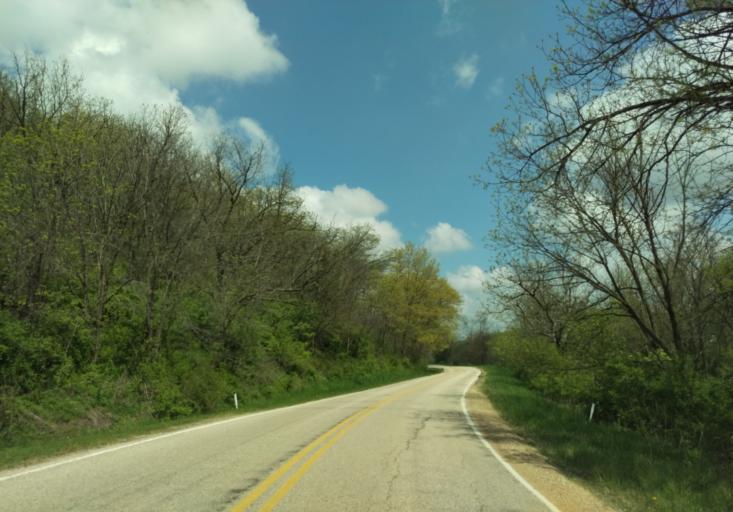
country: US
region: Wisconsin
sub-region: Dane County
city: Mount Horeb
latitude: 43.0646
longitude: -89.7957
